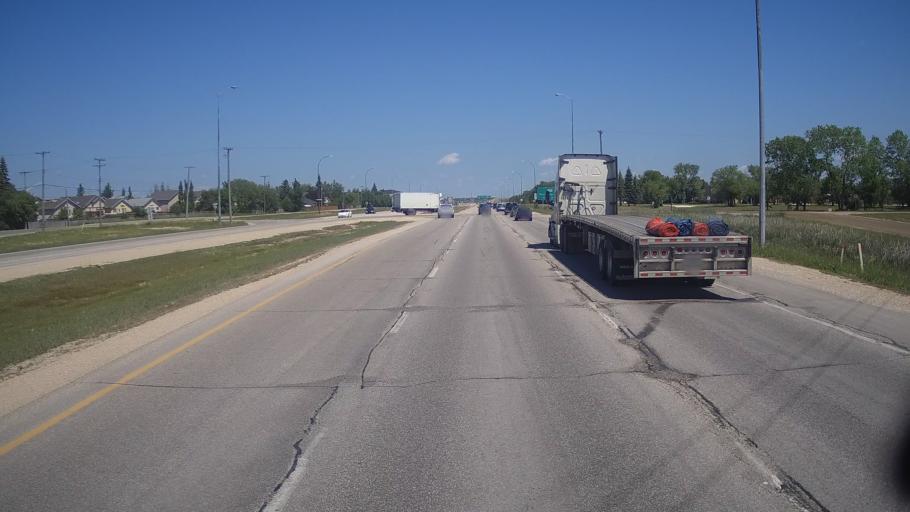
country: CA
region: Manitoba
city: Winnipeg
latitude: 49.9366
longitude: -97.0394
